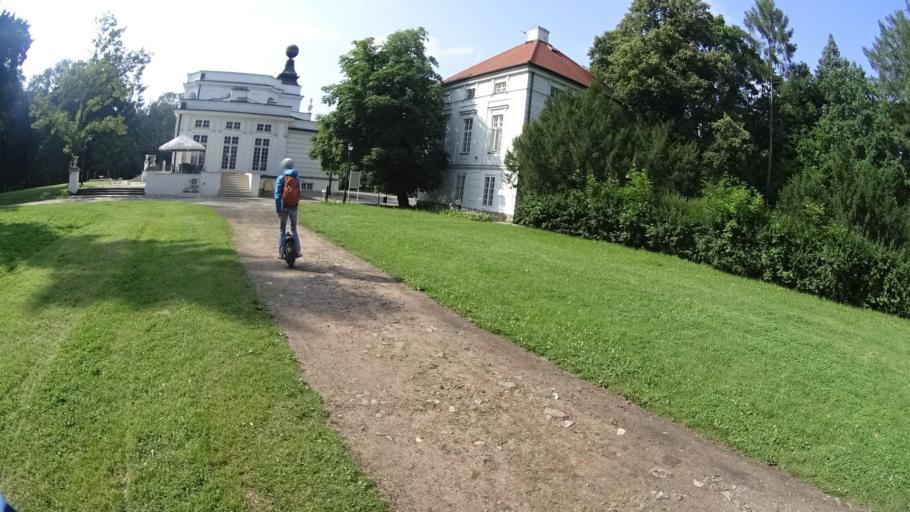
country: PL
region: Masovian Voivodeship
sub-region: Powiat legionowski
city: Jablonna
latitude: 52.3744
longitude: 20.9148
